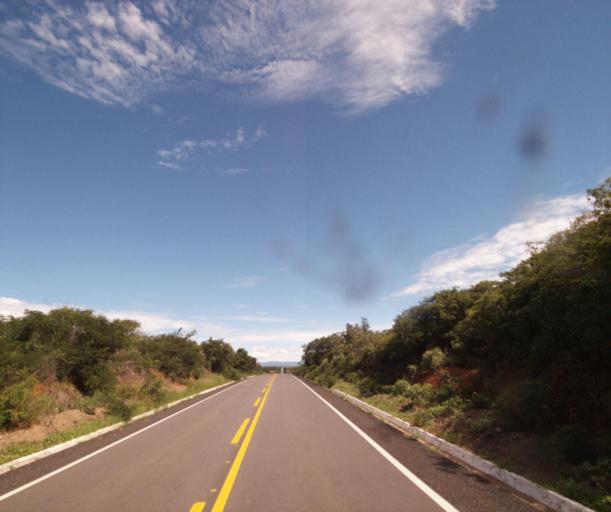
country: BR
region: Bahia
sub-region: Guanambi
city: Guanambi
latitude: -14.3906
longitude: -42.7593
